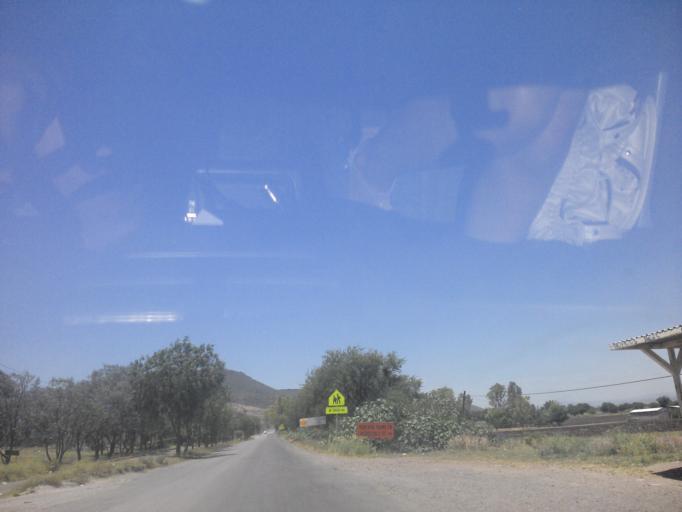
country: MX
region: Guanajuato
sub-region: San Francisco del Rincon
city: San Ignacio de Hidalgo
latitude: 20.9221
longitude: -101.9173
